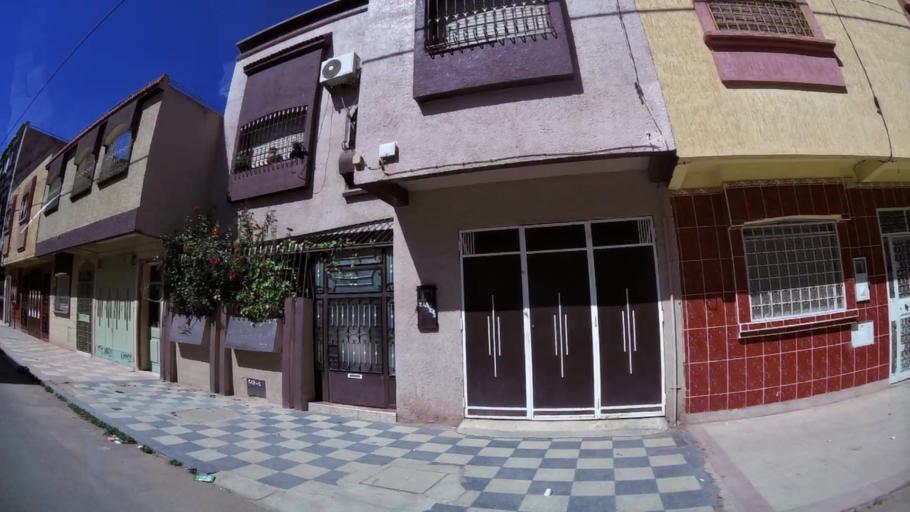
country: MA
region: Oriental
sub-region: Oujda-Angad
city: Oujda
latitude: 34.6856
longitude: -1.9432
